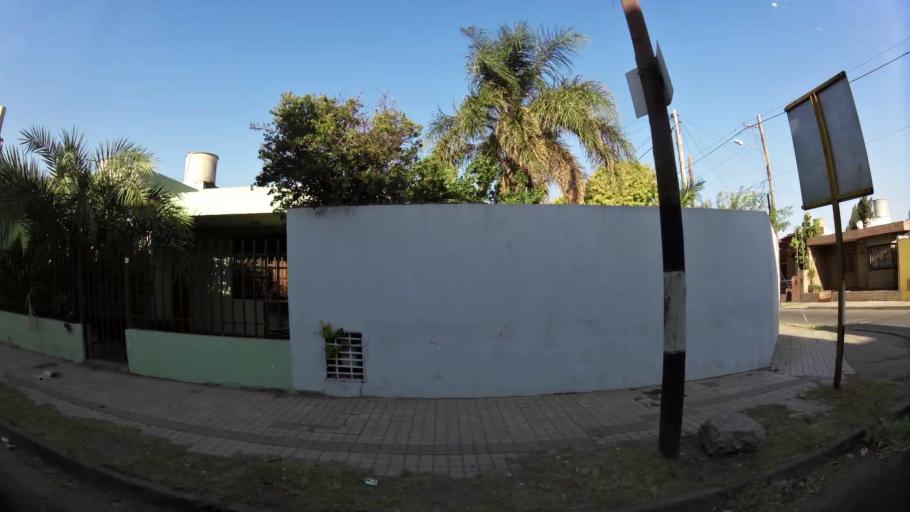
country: AR
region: Cordoba
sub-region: Departamento de Capital
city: Cordoba
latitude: -31.4337
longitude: -64.2480
